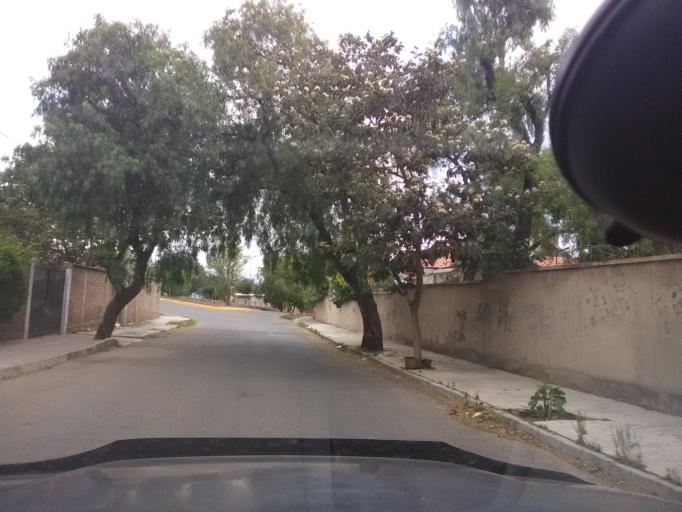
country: BO
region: Cochabamba
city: Cochabamba
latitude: -17.3624
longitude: -66.1696
